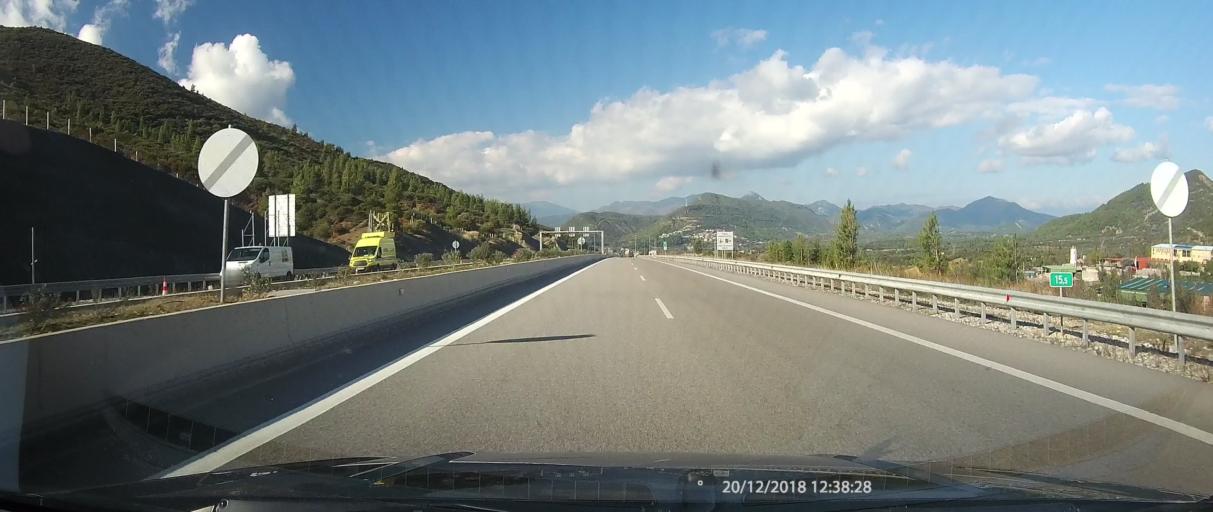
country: GR
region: West Greece
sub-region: Nomos Aitolias kai Akarnanias
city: Galatas
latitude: 38.3603
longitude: 21.6553
